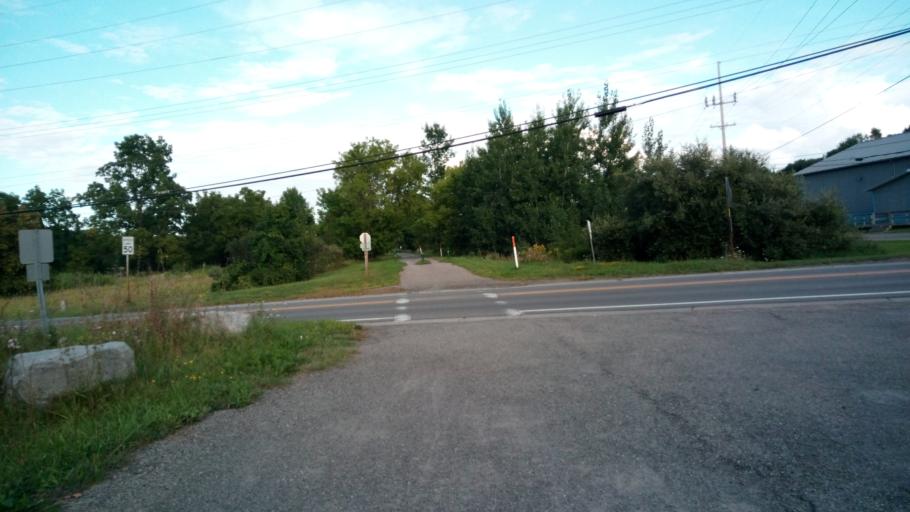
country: US
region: New York
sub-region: Ontario County
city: Victor
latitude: 43.0005
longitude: -77.4553
